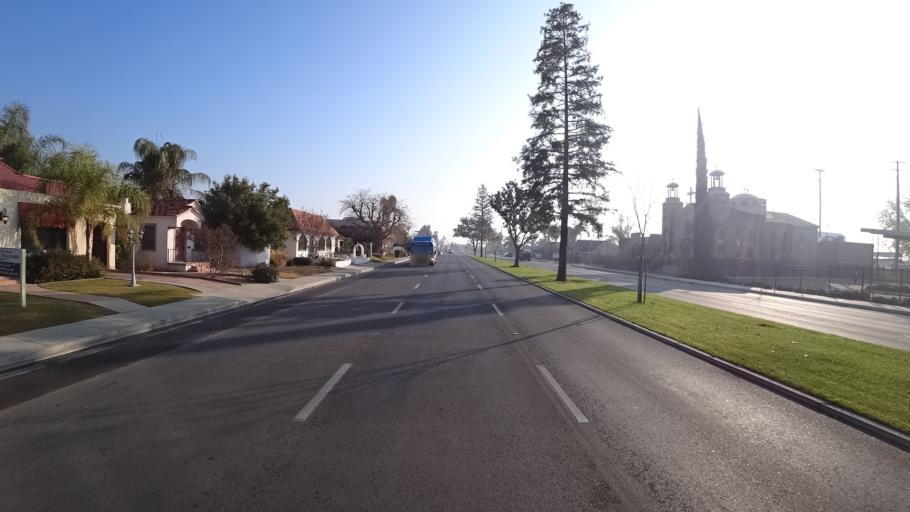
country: US
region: California
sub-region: Kern County
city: Bakersfield
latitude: 35.3733
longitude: -119.0068
